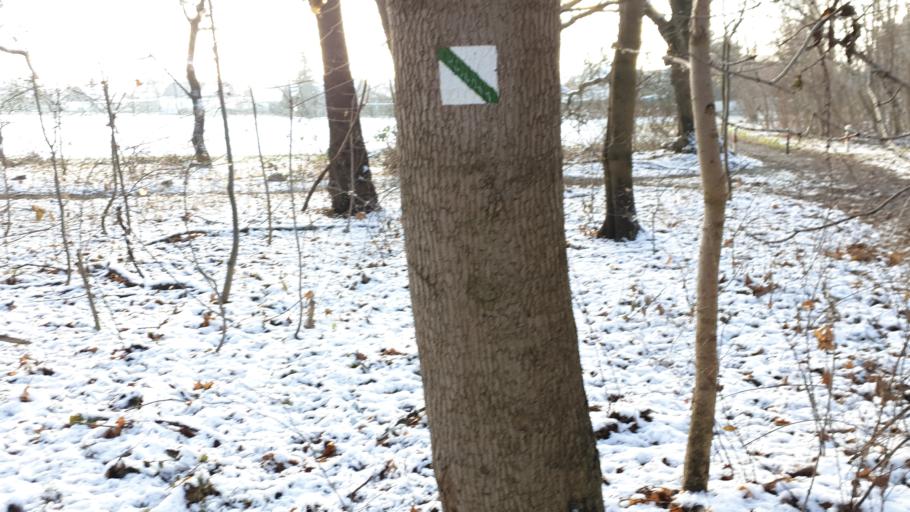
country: DE
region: Saxony
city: Taucha
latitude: 51.3894
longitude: 12.4600
